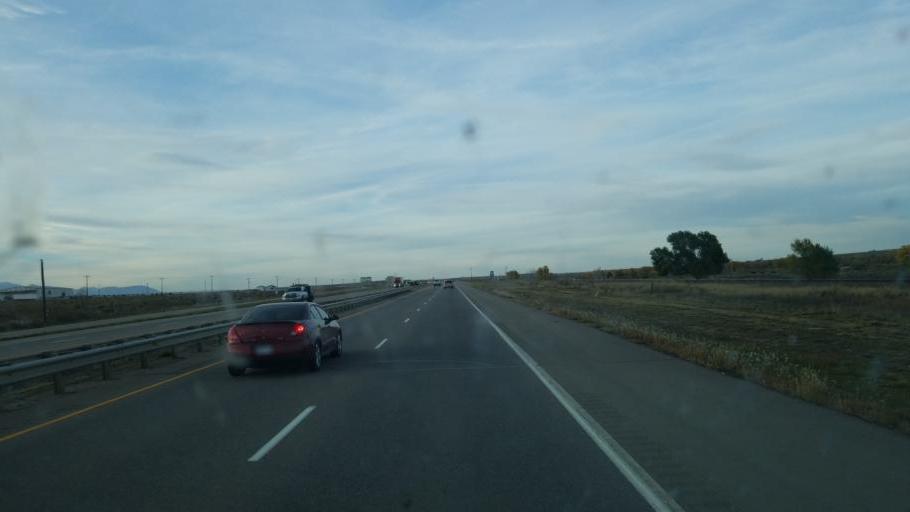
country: US
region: Colorado
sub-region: Pueblo County
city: Pueblo
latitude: 38.3484
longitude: -104.6200
